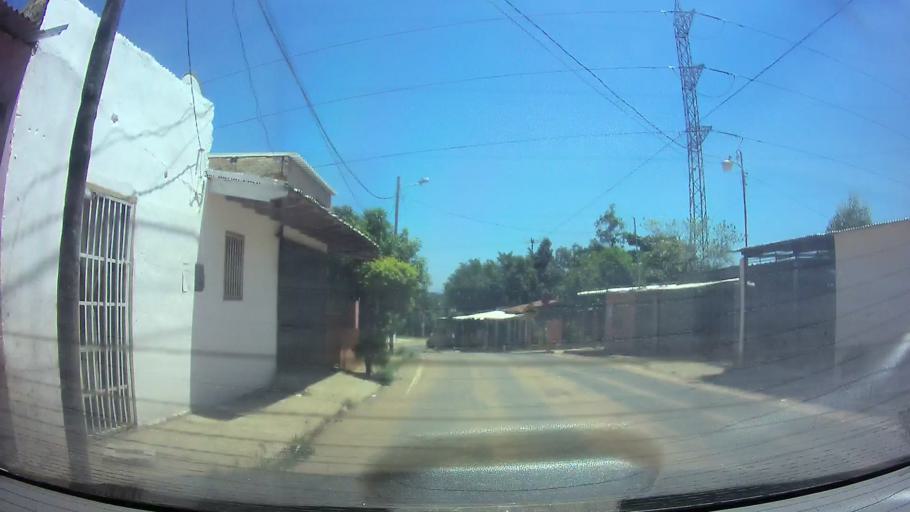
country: PY
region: Central
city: San Lorenzo
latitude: -25.3300
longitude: -57.4864
